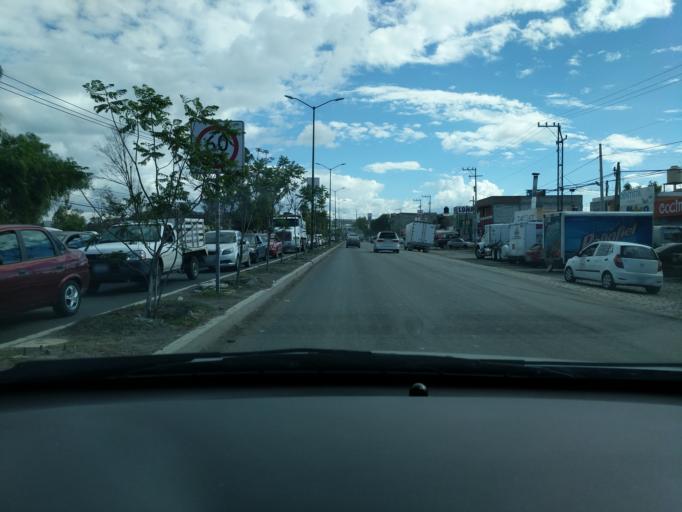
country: MX
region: Queretaro
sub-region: El Marques
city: General Lazaro Cardenas (El Colorado)
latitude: 20.5776
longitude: -100.2564
